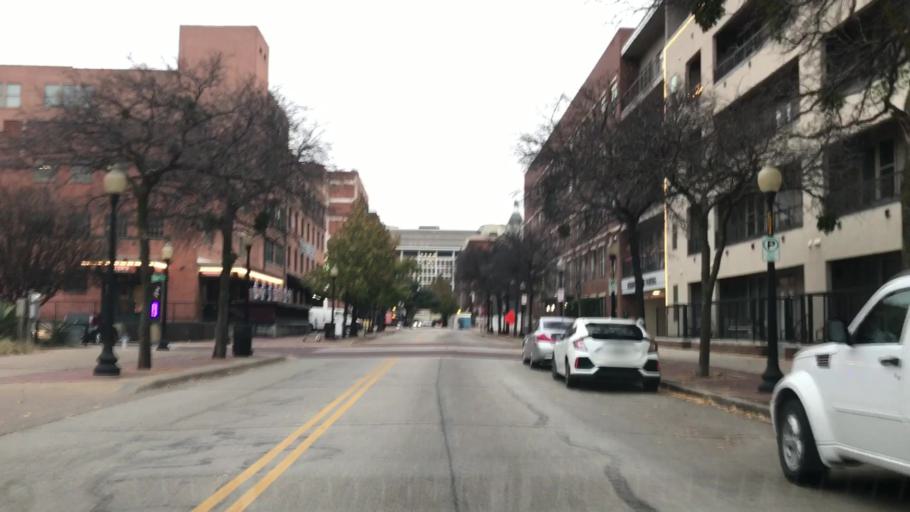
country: US
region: Texas
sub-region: Dallas County
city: Dallas
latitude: 32.7824
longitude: -96.8080
